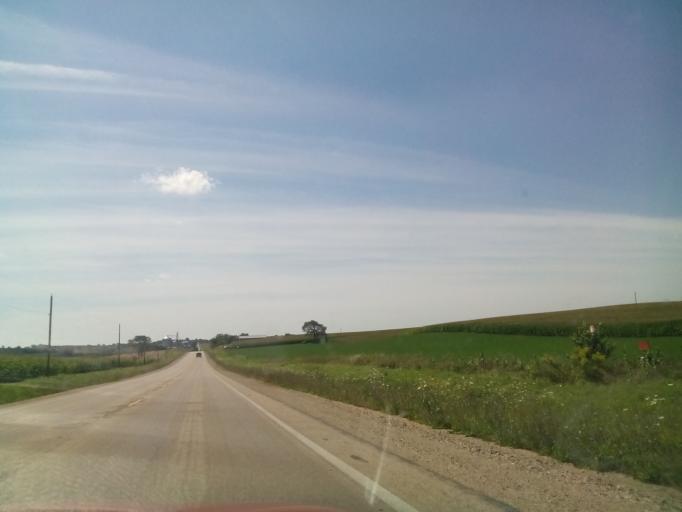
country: US
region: Wisconsin
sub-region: Green County
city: Monticello
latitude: 42.7261
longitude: -89.5986
